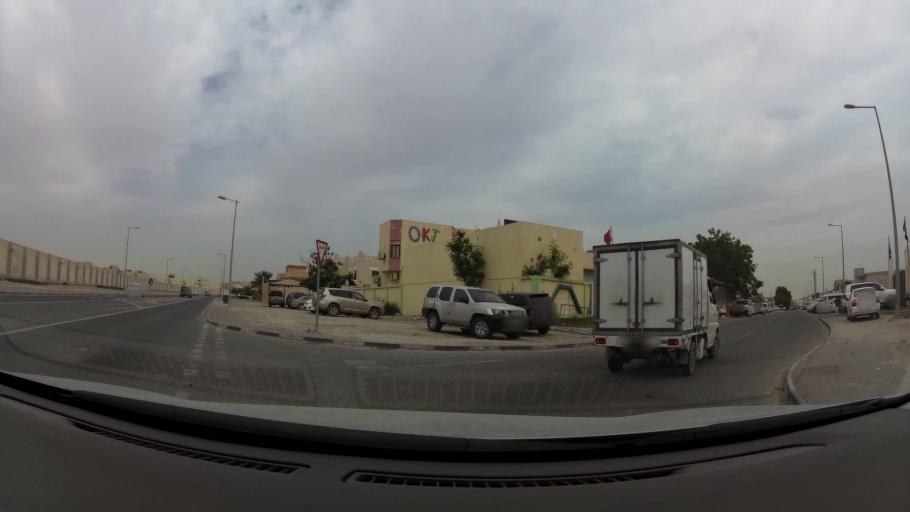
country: QA
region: Baladiyat ar Rayyan
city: Ar Rayyan
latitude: 25.2494
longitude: 51.4380
